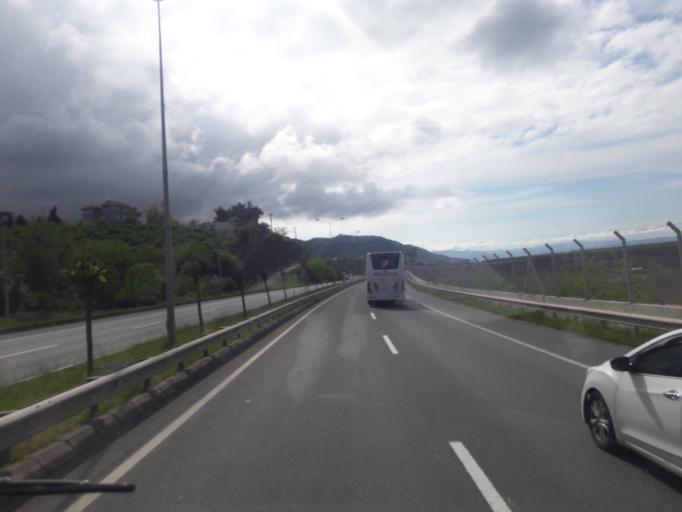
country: TR
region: Giresun
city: Piraziz
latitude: 40.9627
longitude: 38.0920
